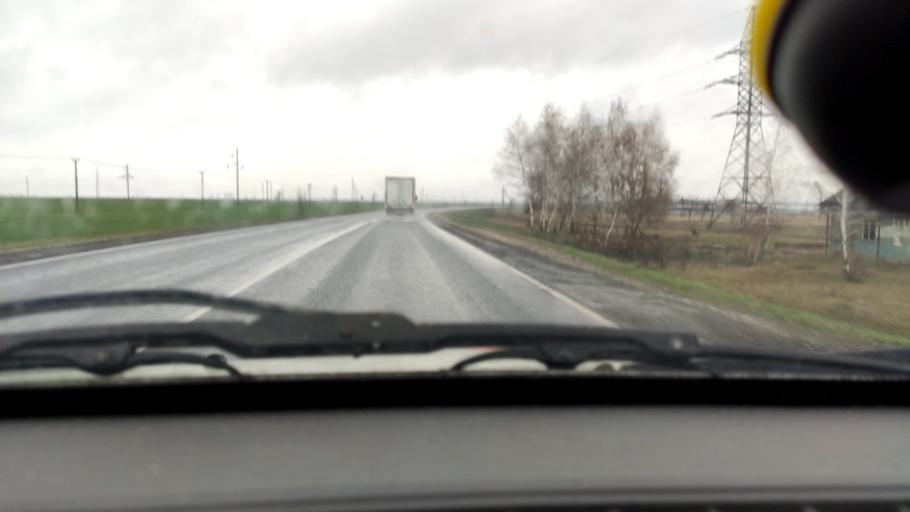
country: RU
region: Samara
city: Povolzhskiy
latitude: 53.6332
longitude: 49.6588
